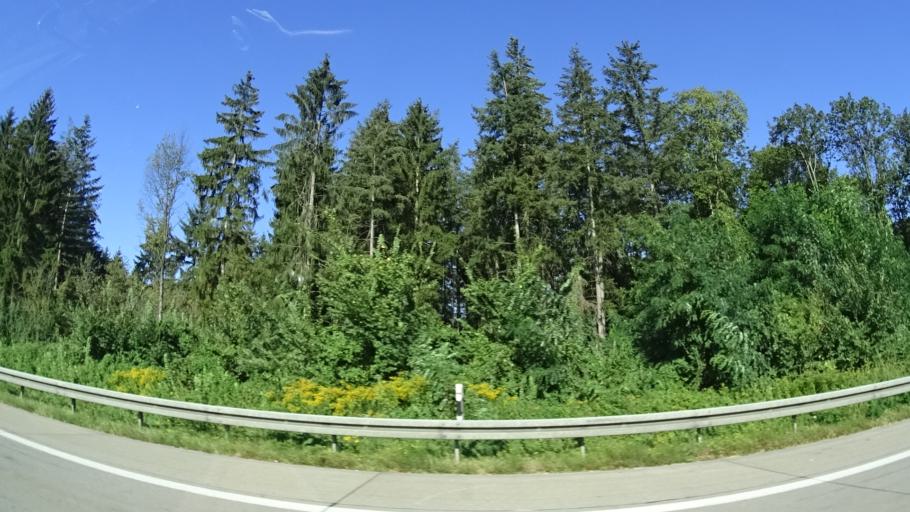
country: DE
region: Baden-Wuerttemberg
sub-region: Karlsruhe Region
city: Weingarten
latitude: 49.0401
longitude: 8.4873
